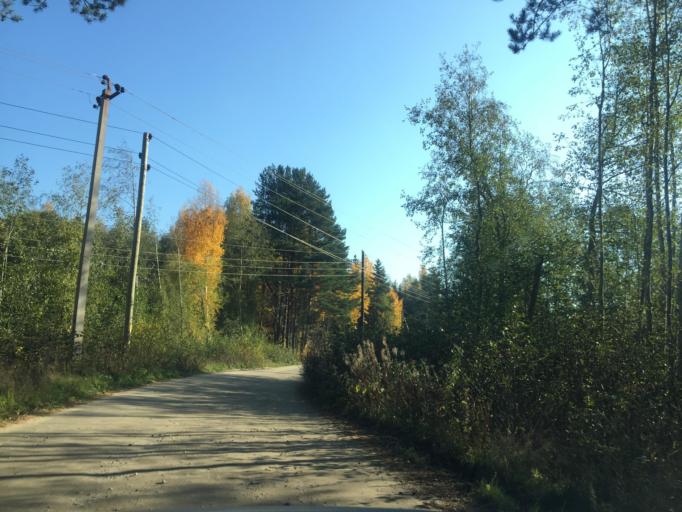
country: RU
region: Leningrad
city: Priozersk
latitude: 61.2918
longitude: 30.0763
